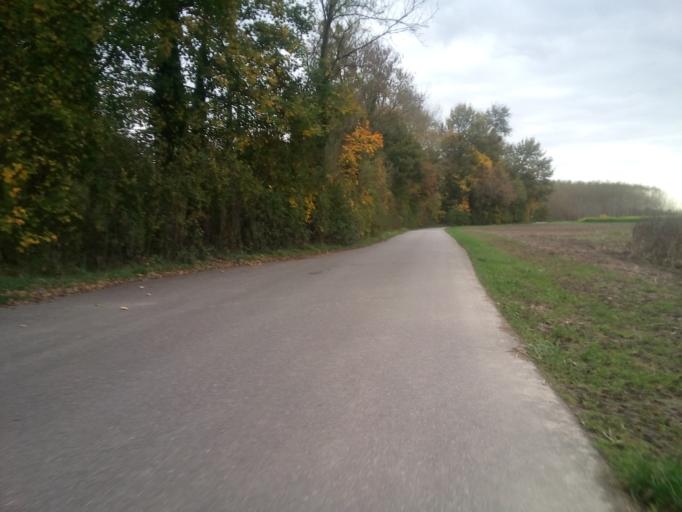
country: DE
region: Baden-Wuerttemberg
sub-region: Karlsruhe Region
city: Schwarzach
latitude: 48.7662
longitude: 8.0382
